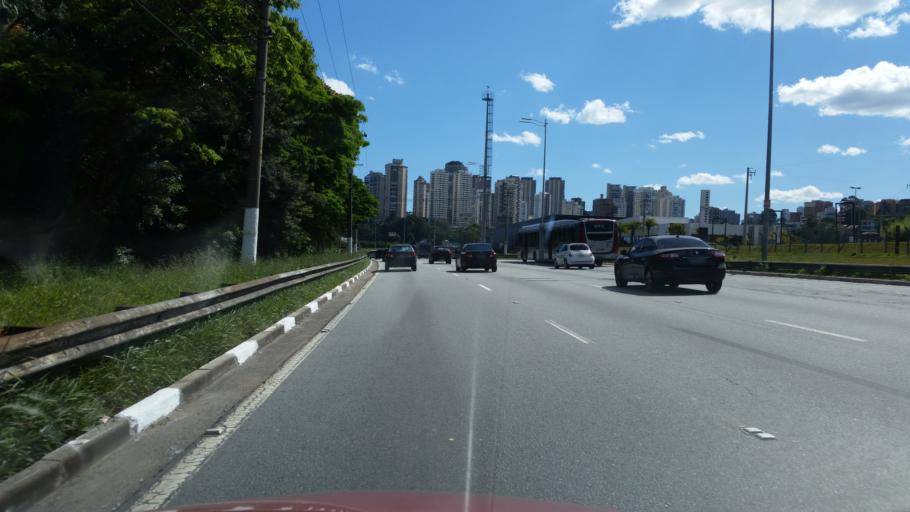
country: BR
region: Sao Paulo
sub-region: Taboao Da Serra
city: Taboao da Serra
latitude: -23.6238
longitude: -46.7097
